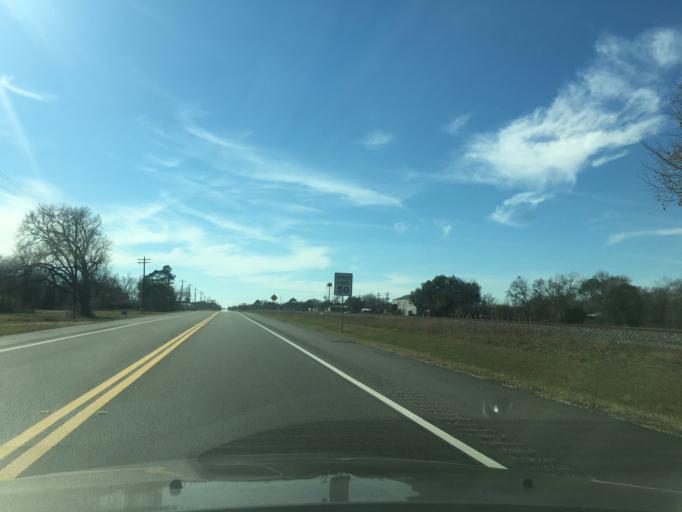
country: US
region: Texas
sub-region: Wharton County
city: East Bernard
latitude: 29.4512
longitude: -95.9942
